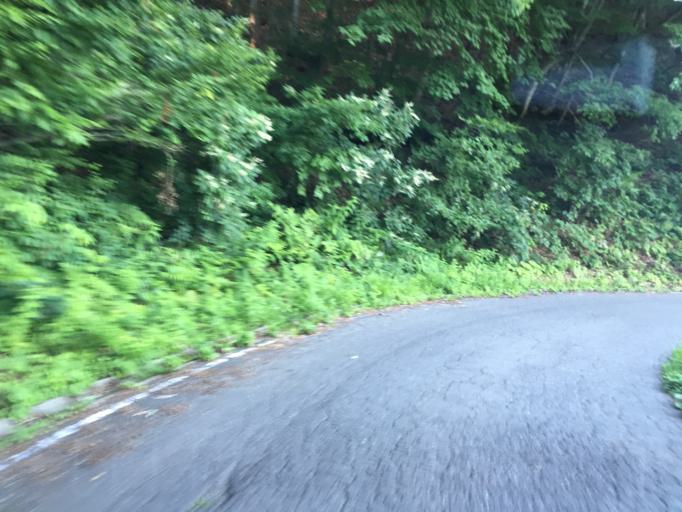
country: JP
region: Yamagata
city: Takahata
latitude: 37.9714
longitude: 140.3179
